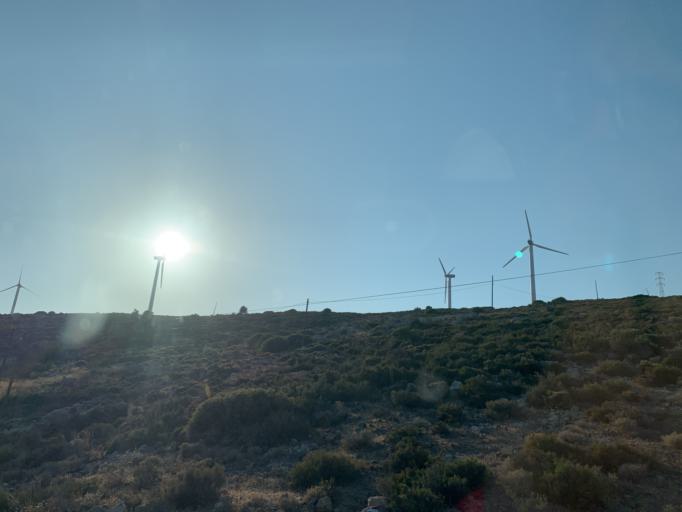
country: TR
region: Izmir
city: Alacati
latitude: 38.2829
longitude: 26.4020
